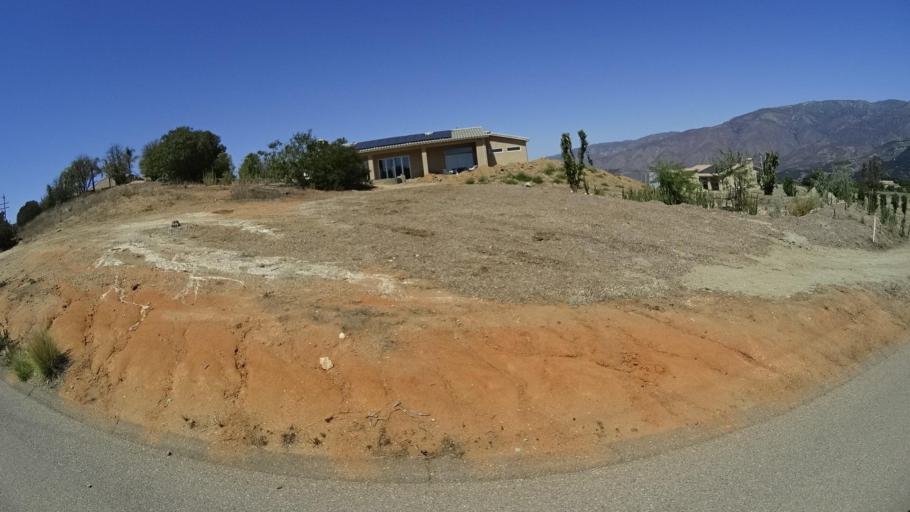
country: US
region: California
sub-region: San Diego County
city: Valley Center
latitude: 33.2864
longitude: -116.9866
